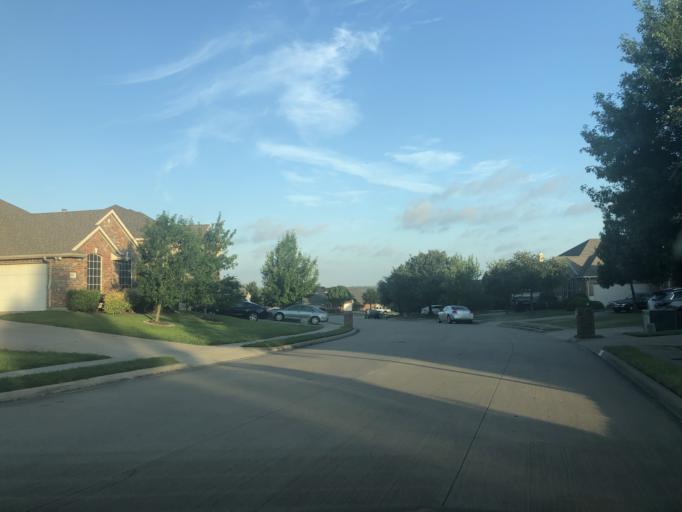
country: US
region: Texas
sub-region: Dallas County
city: Duncanville
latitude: 32.6526
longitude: -96.9670
